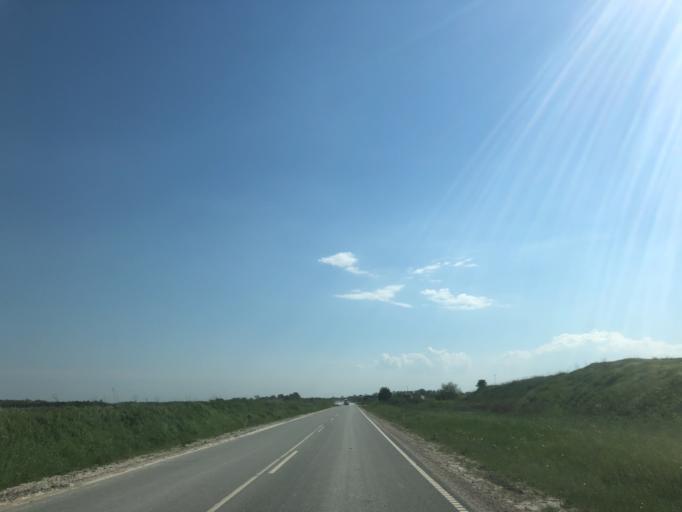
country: DK
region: Zealand
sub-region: Roskilde Kommune
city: Vindinge
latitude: 55.6240
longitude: 12.1205
